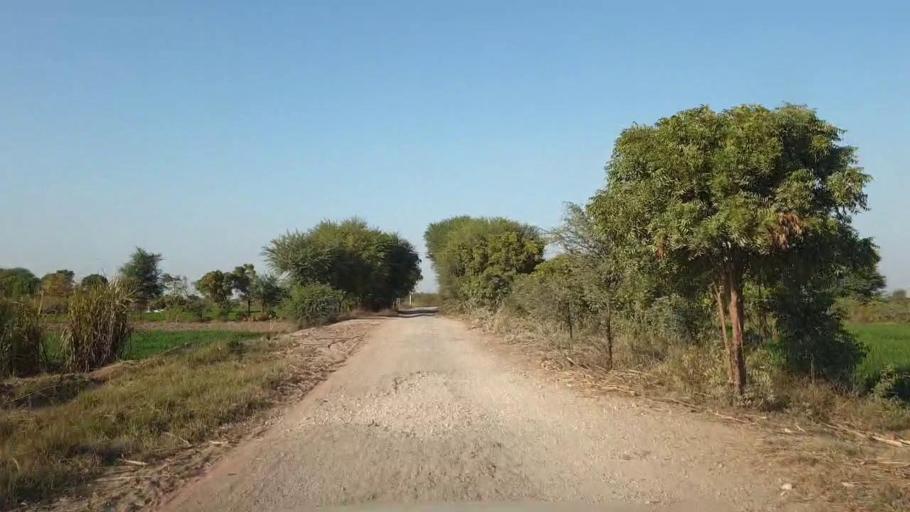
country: PK
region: Sindh
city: Tando Allahyar
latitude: 25.5006
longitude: 68.6490
